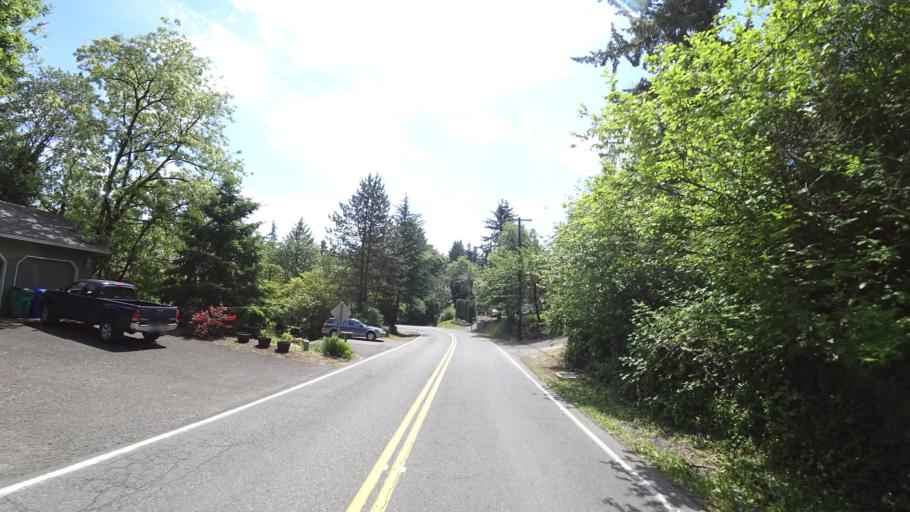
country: US
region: Oregon
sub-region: Washington County
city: Garden Home-Whitford
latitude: 45.4645
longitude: -122.7291
